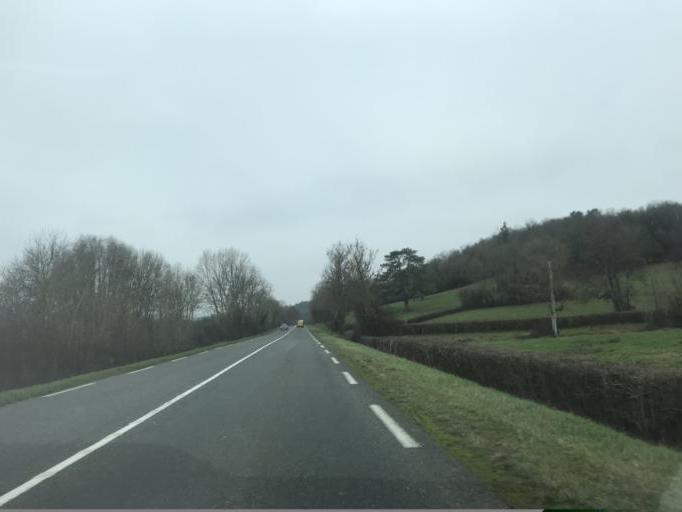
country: FR
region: Bourgogne
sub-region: Departement de l'Yonne
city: Avallon
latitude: 47.5158
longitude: 3.8153
